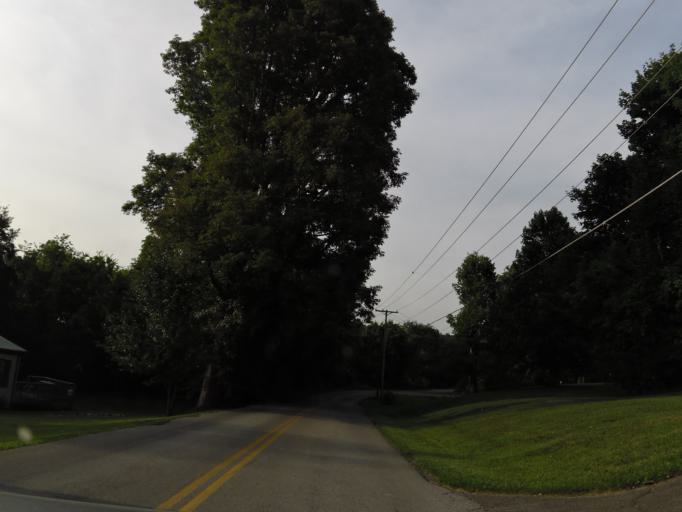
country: US
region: Tennessee
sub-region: Sevier County
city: Seymour
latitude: 35.8605
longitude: -83.7925
